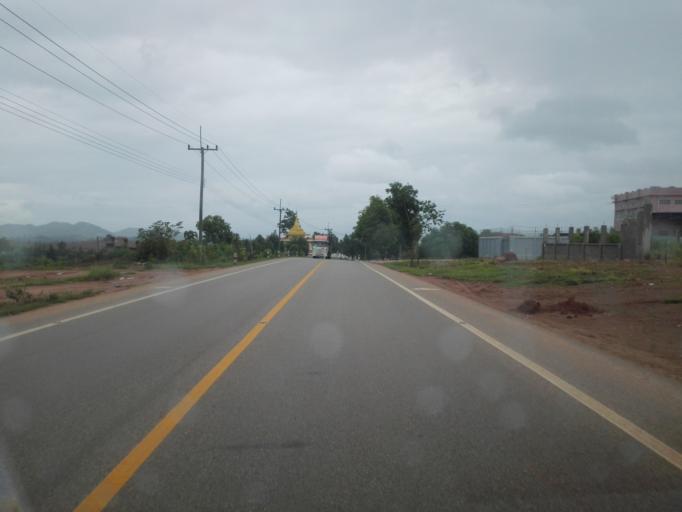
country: TH
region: Tak
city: Mae Sot
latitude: 16.6925
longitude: 98.4579
